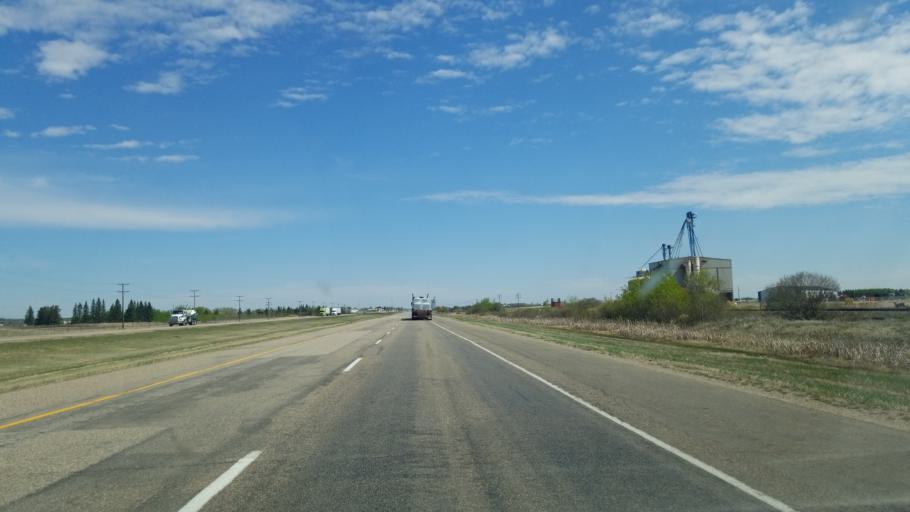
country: CA
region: Saskatchewan
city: Lloydminster
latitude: 53.1364
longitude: -109.6468
